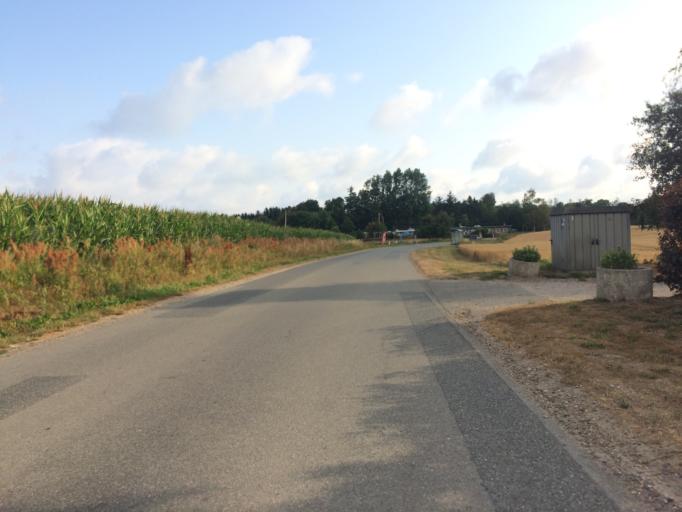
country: DK
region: Central Jutland
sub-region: Holstebro Kommune
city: Vinderup
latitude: 56.6172
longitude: 8.7339
